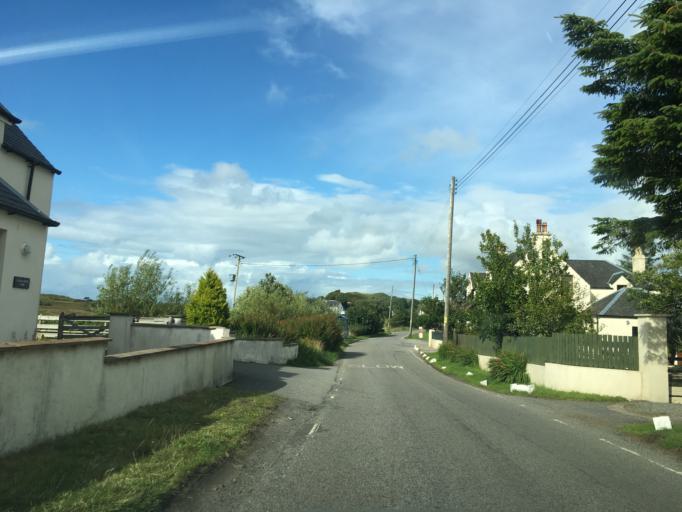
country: GB
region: Scotland
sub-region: Argyll and Bute
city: Oban
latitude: 56.2917
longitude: -5.6149
